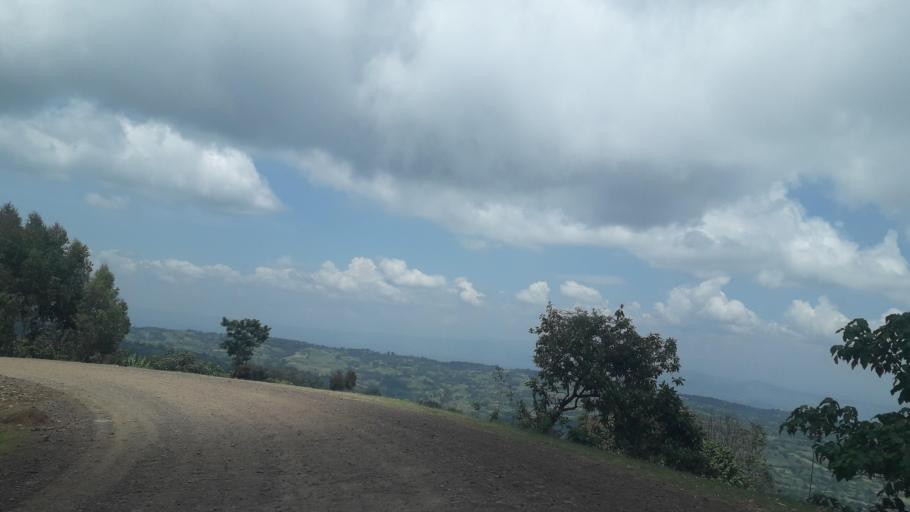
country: ET
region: Oromiya
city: Jima
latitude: 7.4532
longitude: 36.8732
